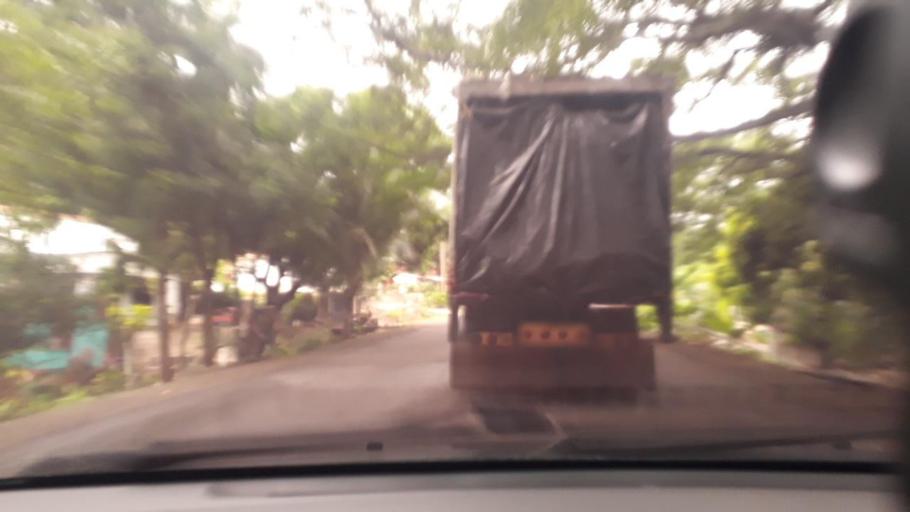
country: GT
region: Jutiapa
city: Atescatempa
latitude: 14.2483
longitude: -89.7139
